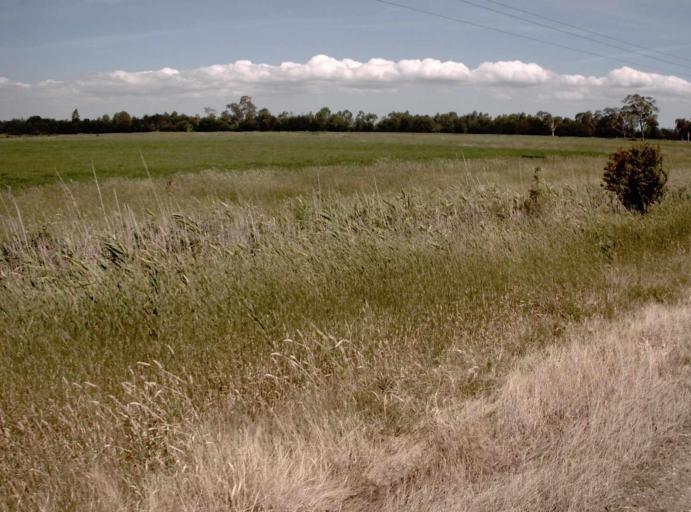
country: AU
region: Victoria
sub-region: Wellington
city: Heyfield
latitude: -38.0019
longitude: 146.8840
